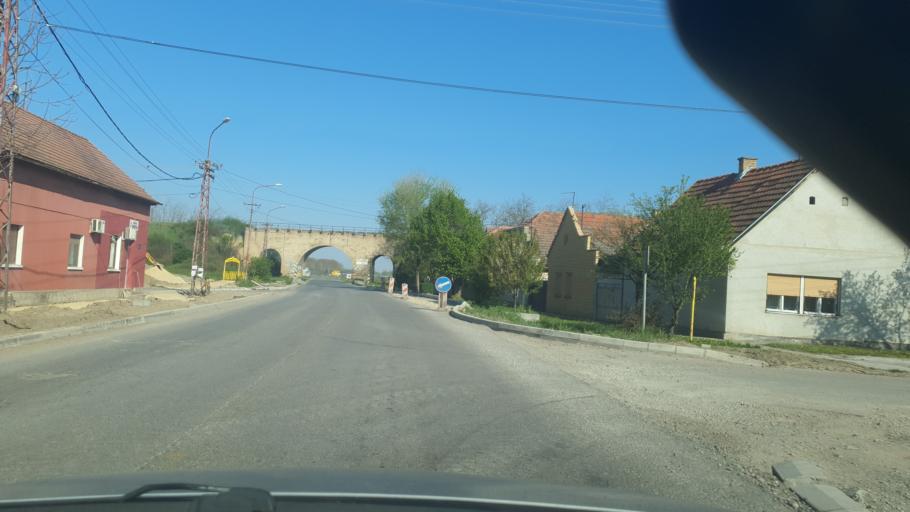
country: RS
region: Autonomna Pokrajina Vojvodina
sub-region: Zapadnobacki Okrug
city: Kula
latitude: 45.6211
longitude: 19.5179
